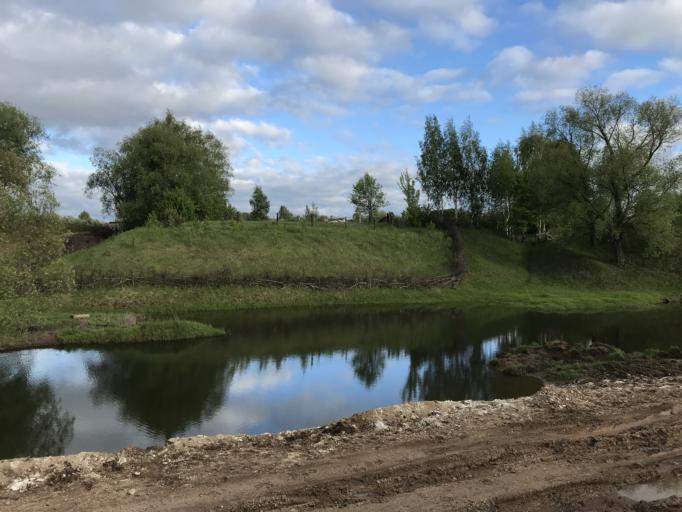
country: RU
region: Chuvashia
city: Kanash
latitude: 55.5402
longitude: 47.4931
